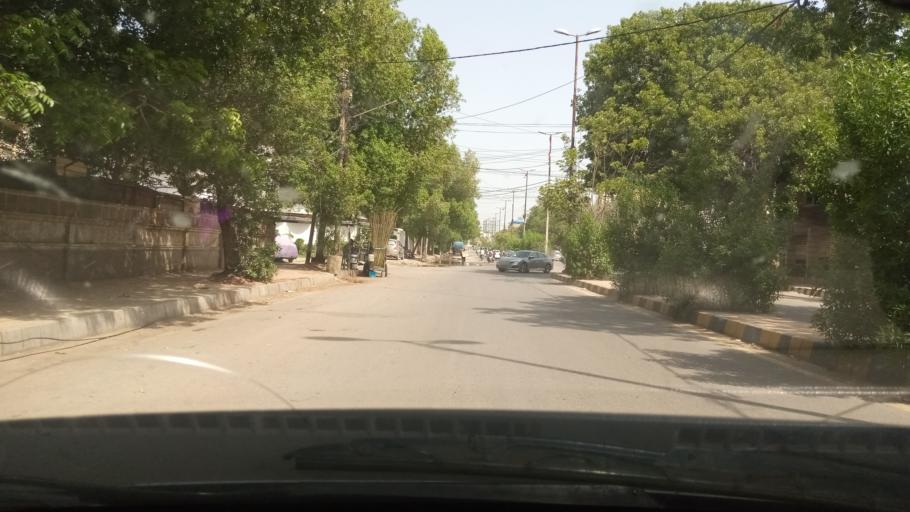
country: PK
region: Sindh
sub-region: Karachi District
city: Karachi
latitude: 24.8757
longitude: 67.0454
